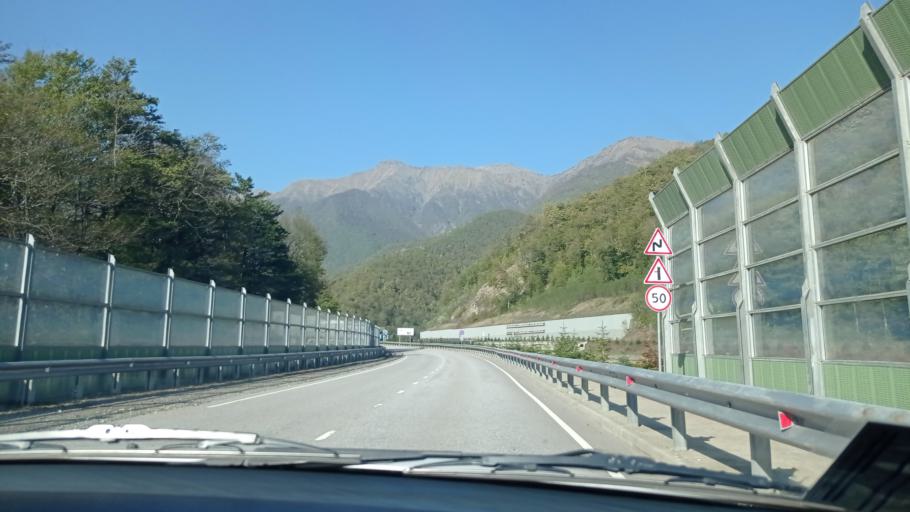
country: RU
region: Krasnodarskiy
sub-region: Sochi City
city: Krasnaya Polyana
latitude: 43.6956
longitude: 40.2693
